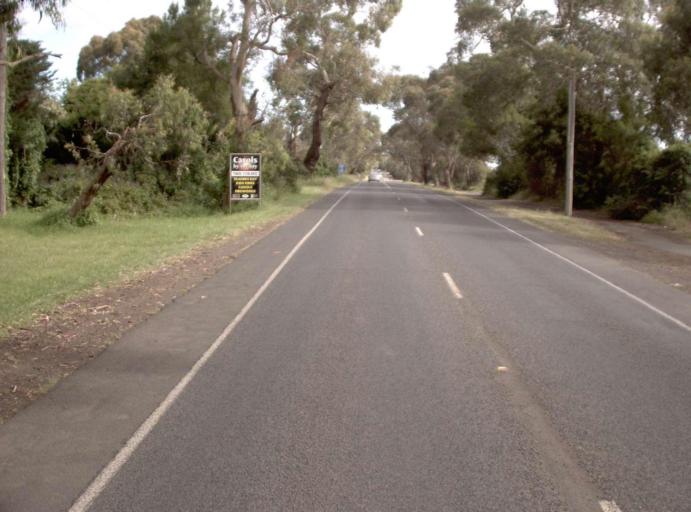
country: AU
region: Victoria
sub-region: Bass Coast
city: Phillip Island
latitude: -38.4715
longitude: 145.2390
